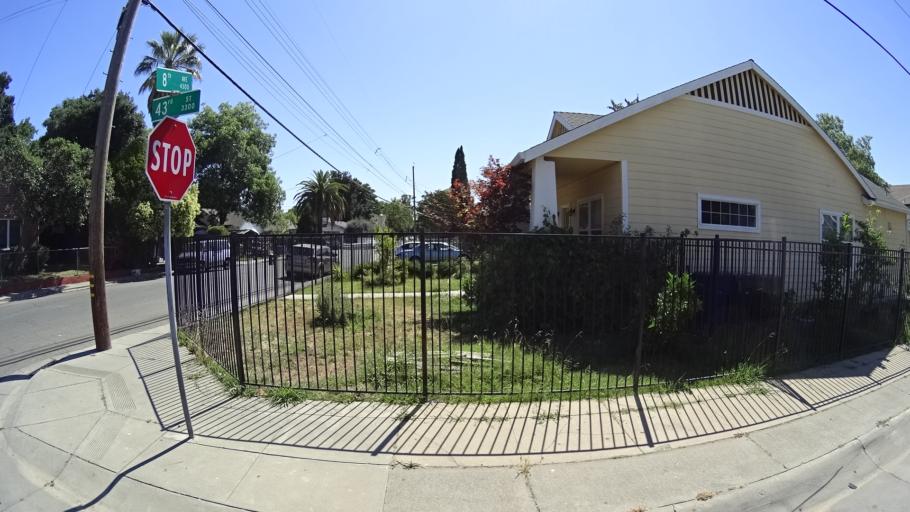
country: US
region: California
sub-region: Sacramento County
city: Parkway
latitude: 38.5444
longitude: -121.4566
